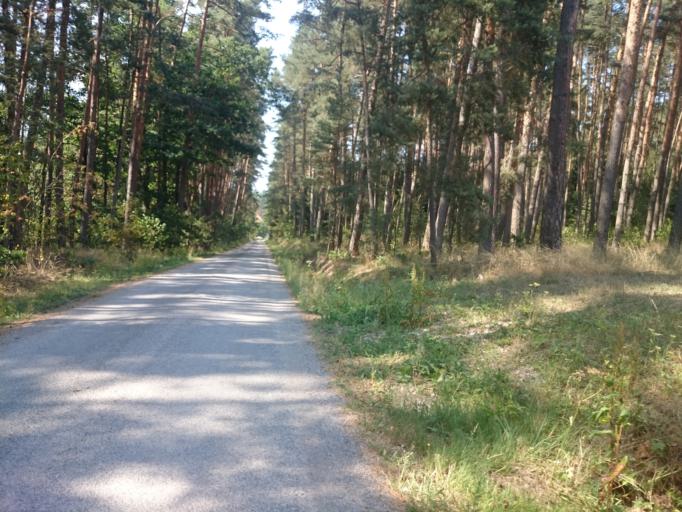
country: DE
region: Bavaria
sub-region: Regierungsbezirk Mittelfranken
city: Hilpoltstein
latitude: 49.1689
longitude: 11.1617
